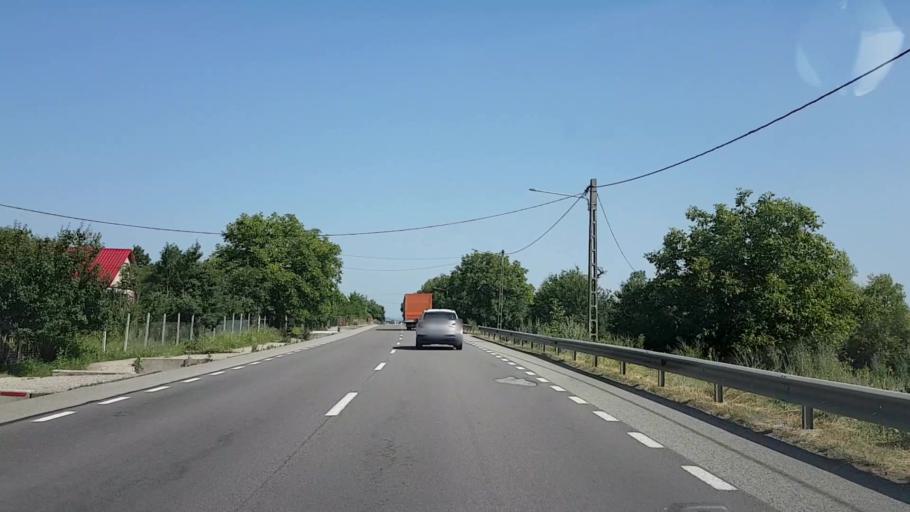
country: RO
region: Bistrita-Nasaud
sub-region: Comuna Sieu-Odorhei
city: Sieu-Odorhei
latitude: 47.1295
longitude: 24.3137
